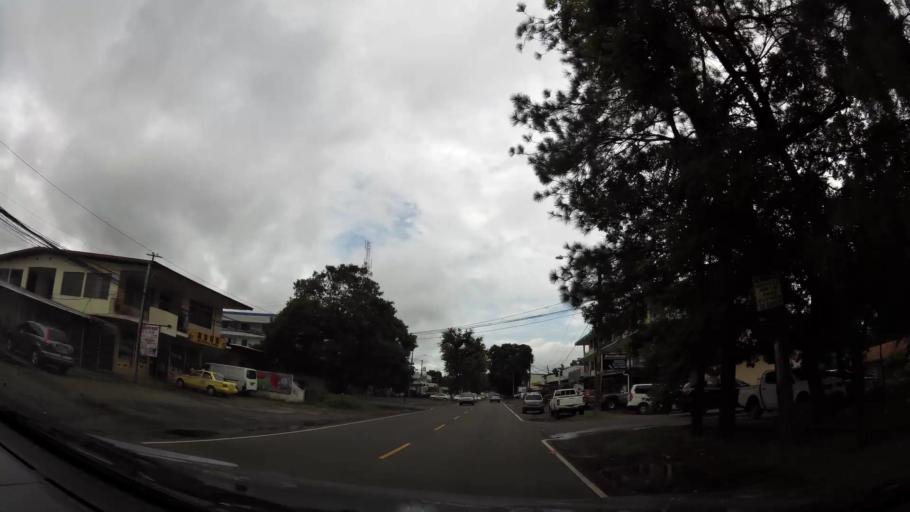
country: PA
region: Chiriqui
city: David
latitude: 8.4397
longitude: -82.4236
